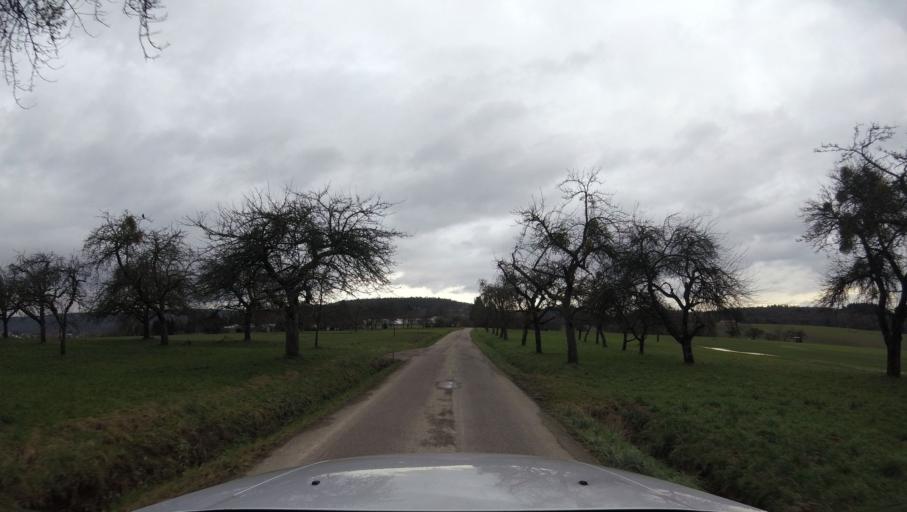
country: DE
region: Baden-Wuerttemberg
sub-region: Regierungsbezirk Stuttgart
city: Aspach
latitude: 48.9738
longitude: 9.4115
